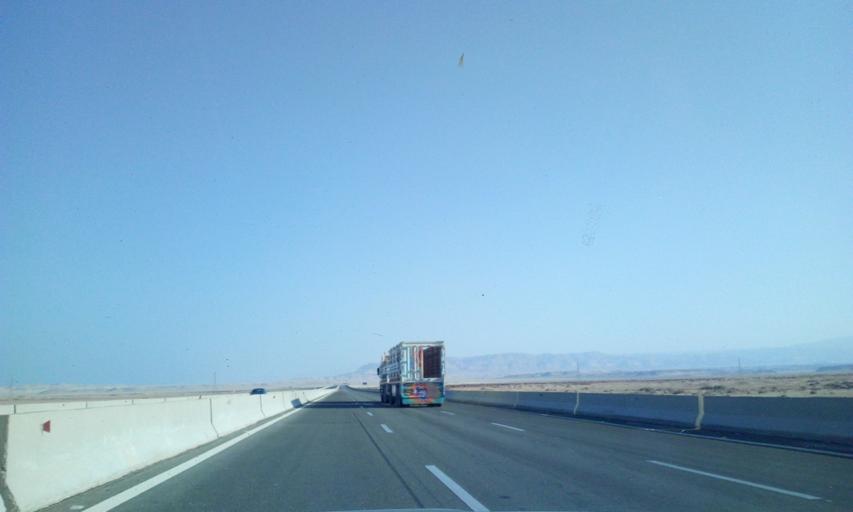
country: EG
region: As Suways
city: Ain Sukhna
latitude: 29.1308
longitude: 32.5240
